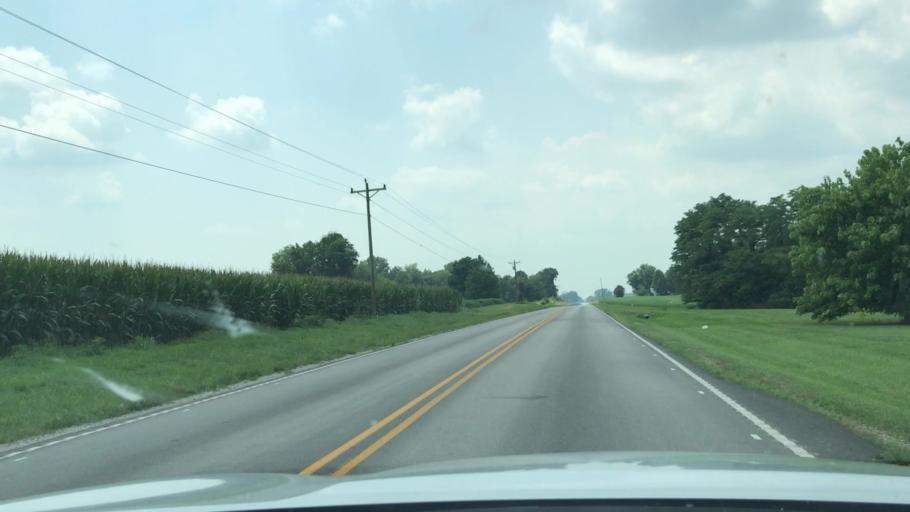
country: US
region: Kentucky
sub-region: Todd County
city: Guthrie
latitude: 36.6896
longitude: -87.1327
